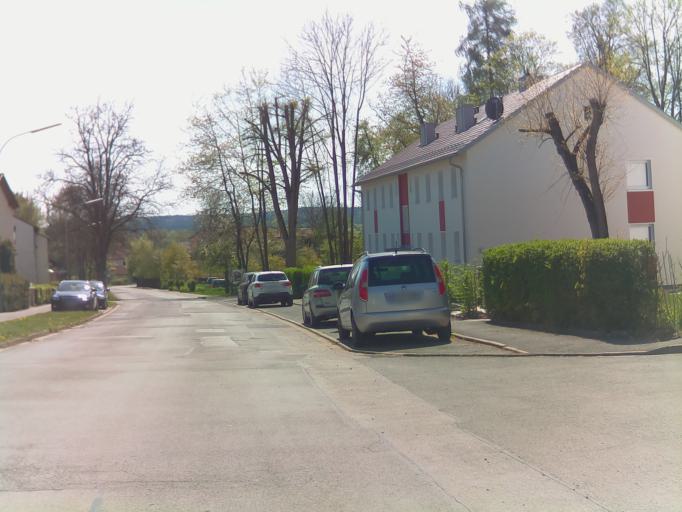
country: DE
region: Thuringia
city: Veilsdorf
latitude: 50.3444
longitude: 10.7770
